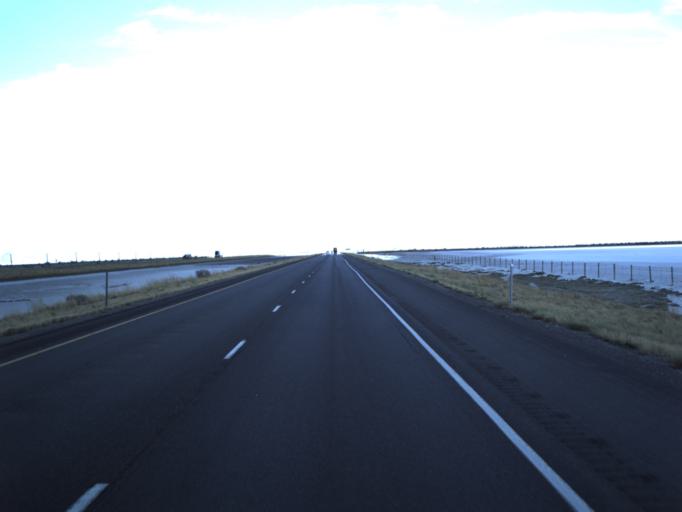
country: US
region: Utah
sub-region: Tooele County
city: Grantsville
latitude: 40.7253
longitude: -112.5733
